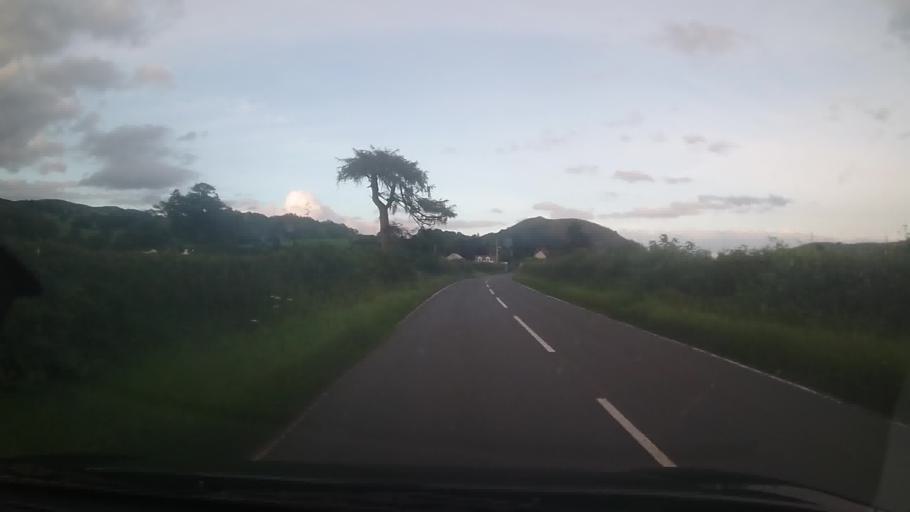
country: GB
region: Wales
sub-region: Sir Powys
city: Llanrhaeadr-ym-Mochnant
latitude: 52.8128
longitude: -3.2538
